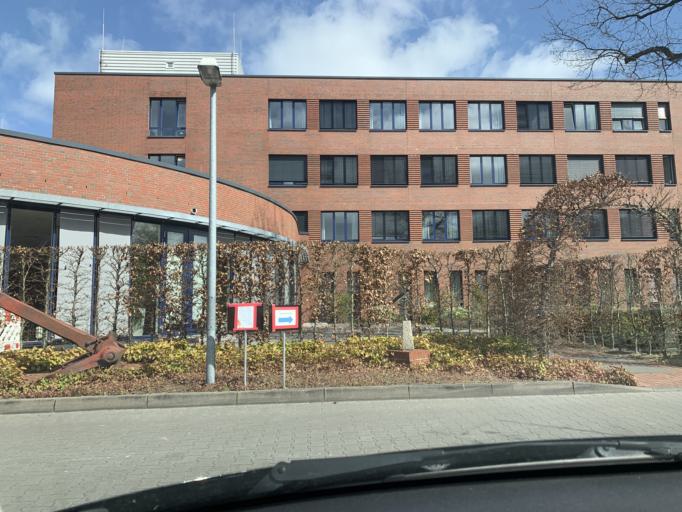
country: DE
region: Lower Saxony
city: Westerstede
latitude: 53.2571
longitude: 7.9176
